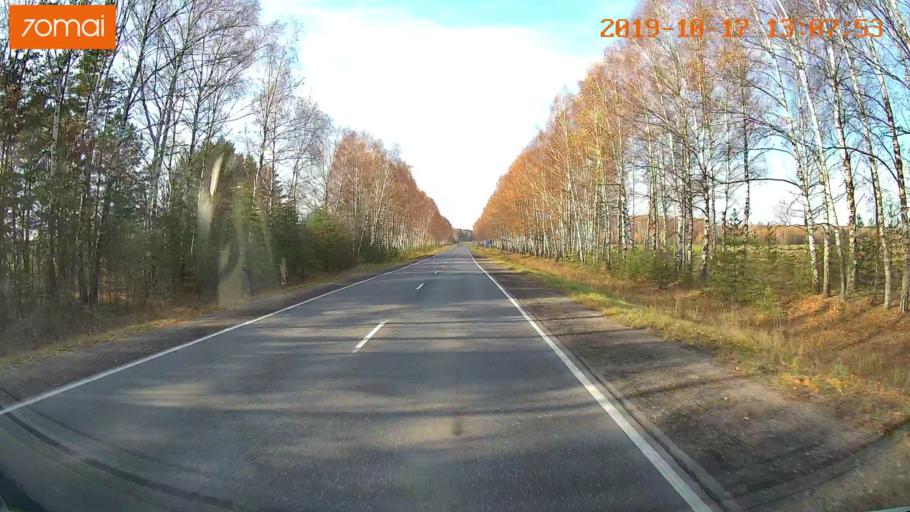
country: RU
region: Rjazan
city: Syntul
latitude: 54.9852
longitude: 41.2802
